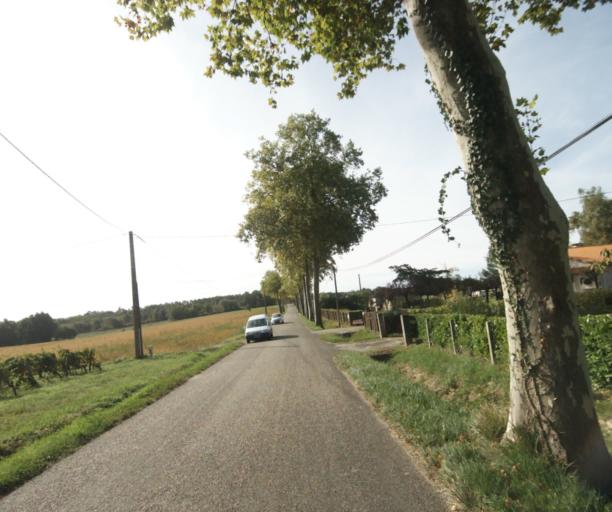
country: FR
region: Midi-Pyrenees
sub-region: Departement du Gers
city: Eauze
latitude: 43.9320
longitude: 0.0921
